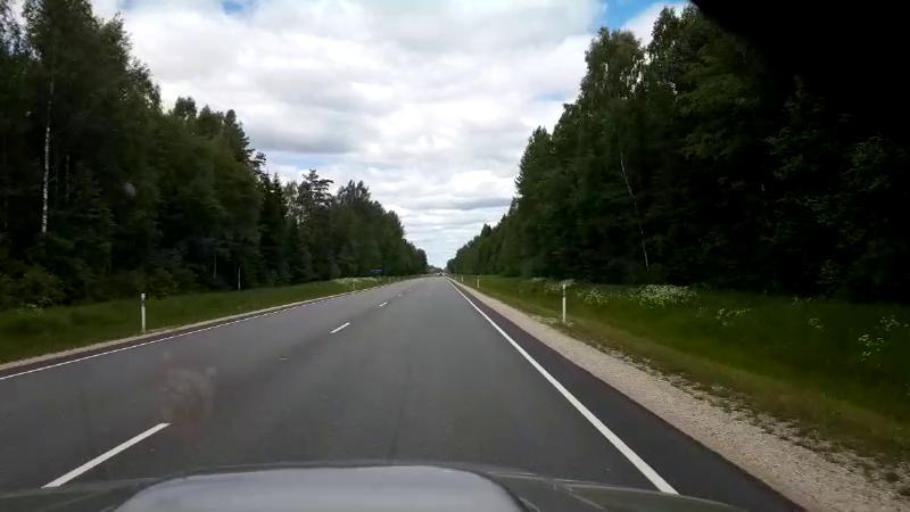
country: EE
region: Raplamaa
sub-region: Maerjamaa vald
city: Marjamaa
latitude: 58.7930
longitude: 24.4130
